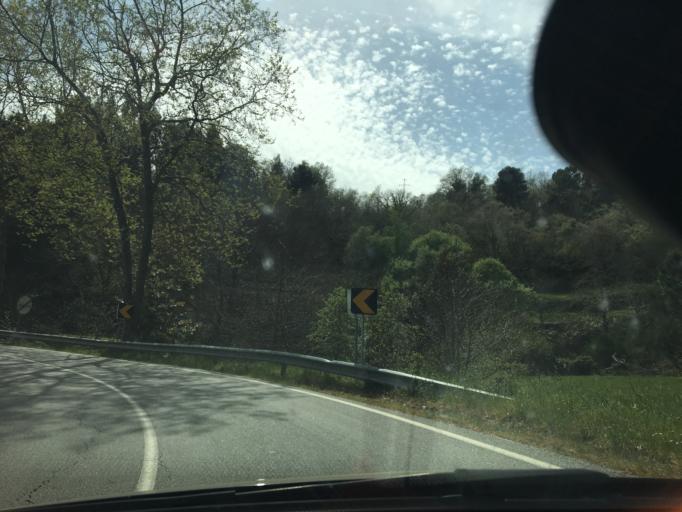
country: PT
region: Vila Real
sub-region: Boticas
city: Boticas
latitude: 41.6889
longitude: -7.6912
